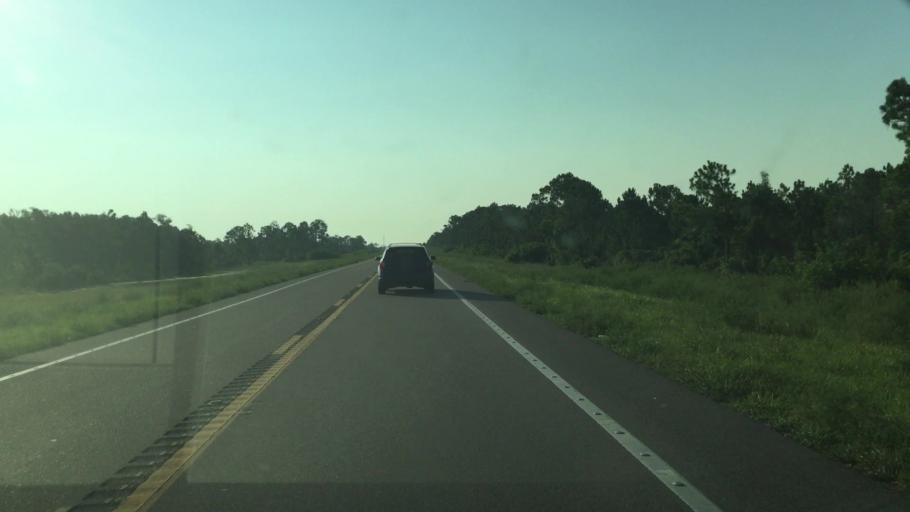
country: US
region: Florida
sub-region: Lee County
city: Lehigh Acres
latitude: 26.5221
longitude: -81.5782
